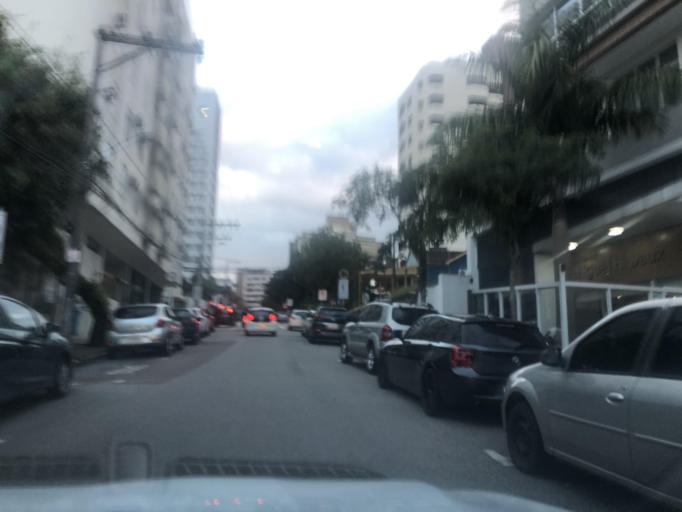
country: BR
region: Santa Catarina
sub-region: Florianopolis
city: Florianopolis
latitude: -27.5925
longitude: -48.5498
